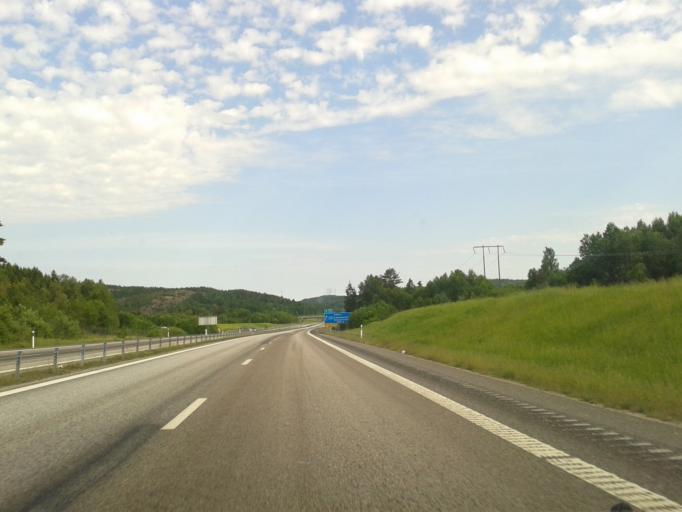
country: SE
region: Vaestra Goetaland
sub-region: Munkedals Kommun
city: Munkedal
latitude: 58.5129
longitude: 11.5545
